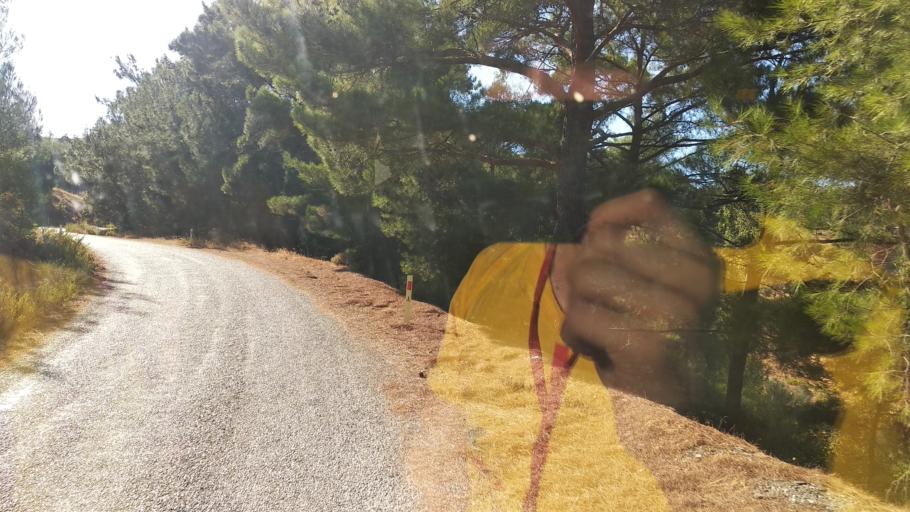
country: TR
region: Izmir
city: Gaziemir
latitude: 38.3274
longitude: 26.9557
